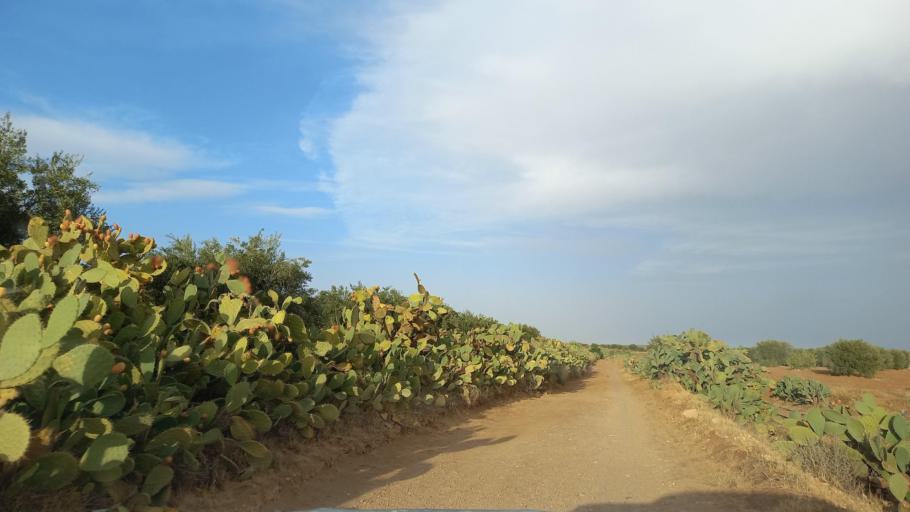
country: TN
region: Al Qasrayn
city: Kasserine
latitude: 35.2246
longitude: 9.0611
